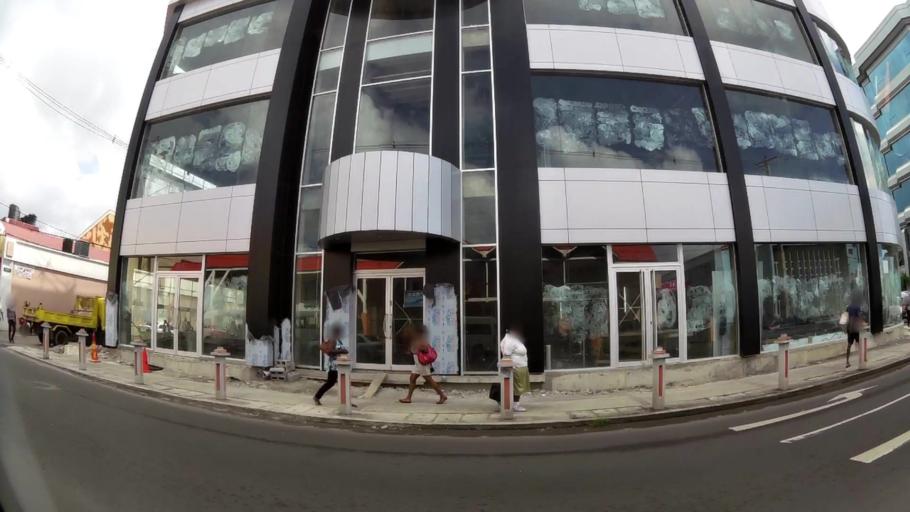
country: LC
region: Castries Quarter
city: Castries
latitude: 14.0110
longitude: -60.9913
